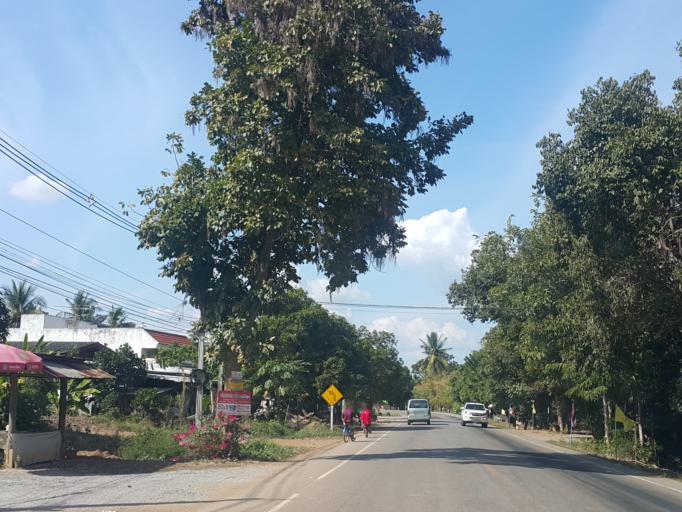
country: TH
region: Sukhothai
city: Sawankhalok
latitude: 17.2911
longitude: 99.8319
